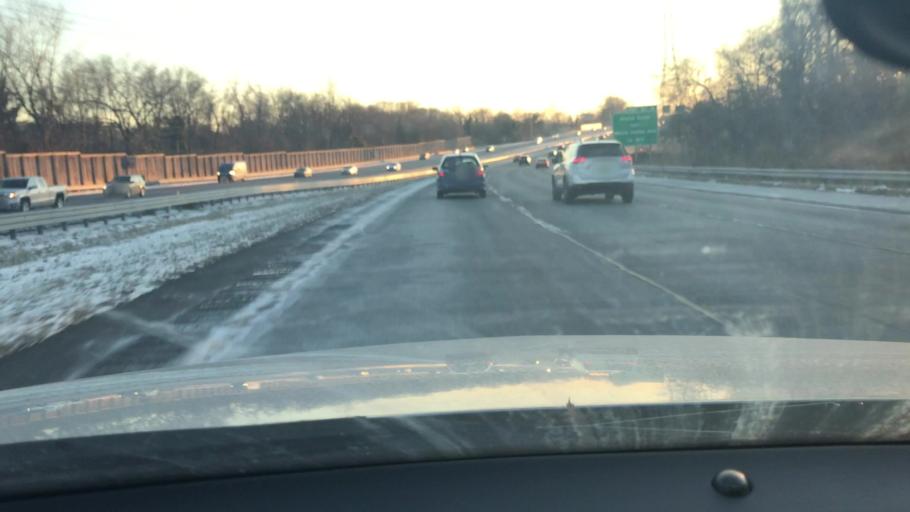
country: US
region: New Jersey
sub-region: Mercer County
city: White Horse
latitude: 40.2033
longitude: -74.7089
